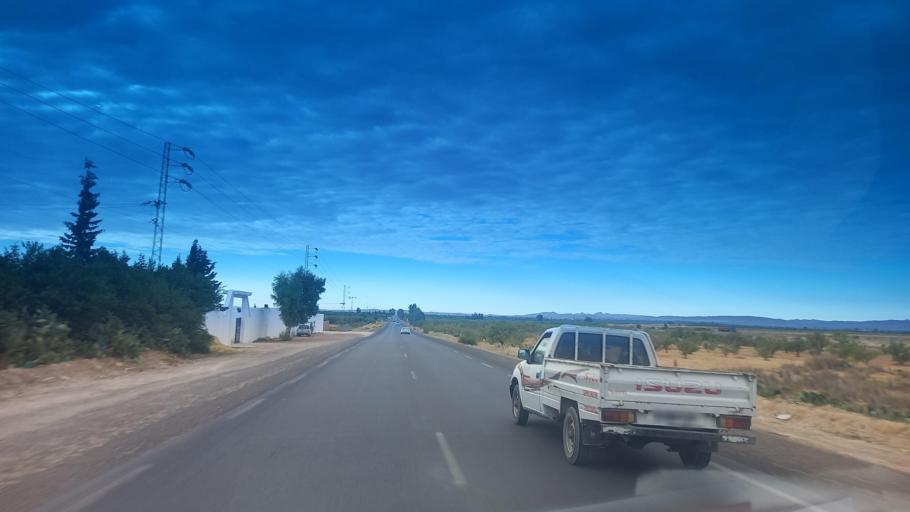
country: TN
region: Al Qasrayn
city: Sbiba
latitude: 35.3130
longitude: 9.0846
